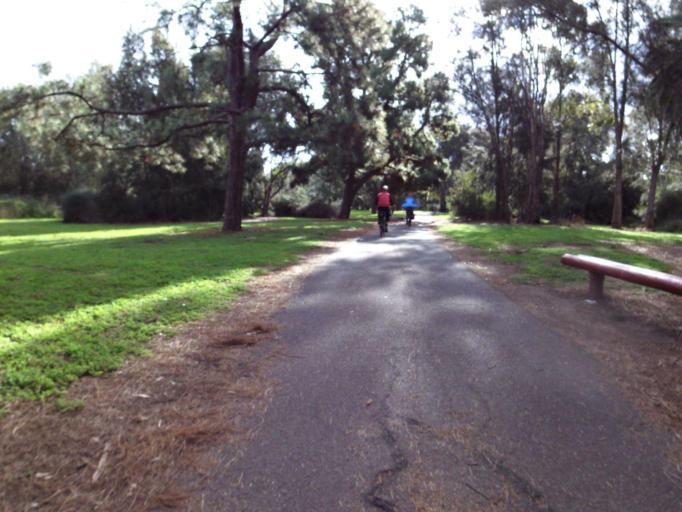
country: AU
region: Victoria
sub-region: Greater Geelong
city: Breakwater
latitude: -38.1668
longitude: 144.3576
